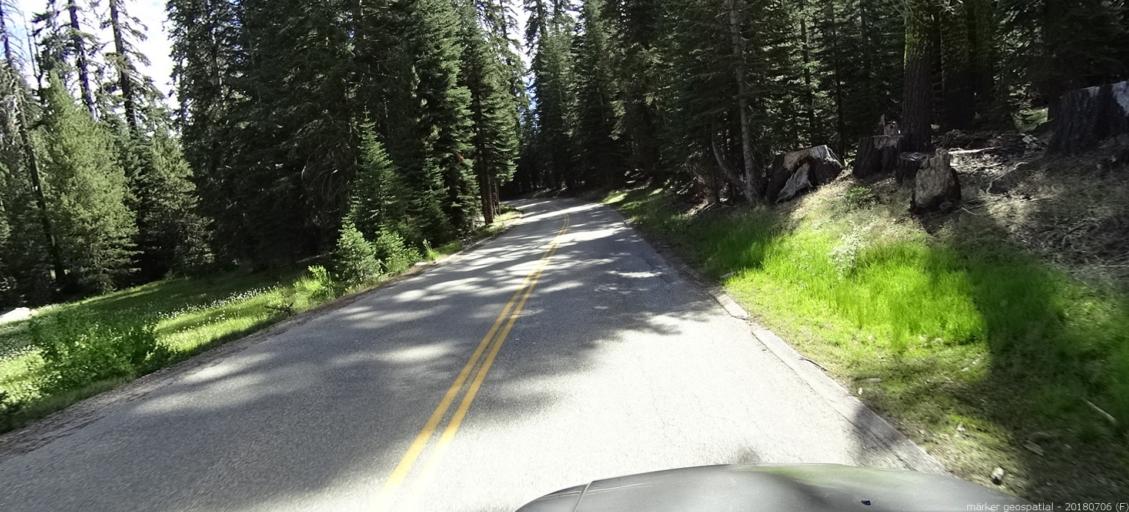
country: US
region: California
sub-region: Madera County
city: Oakhurst
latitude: 37.4138
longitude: -119.4965
